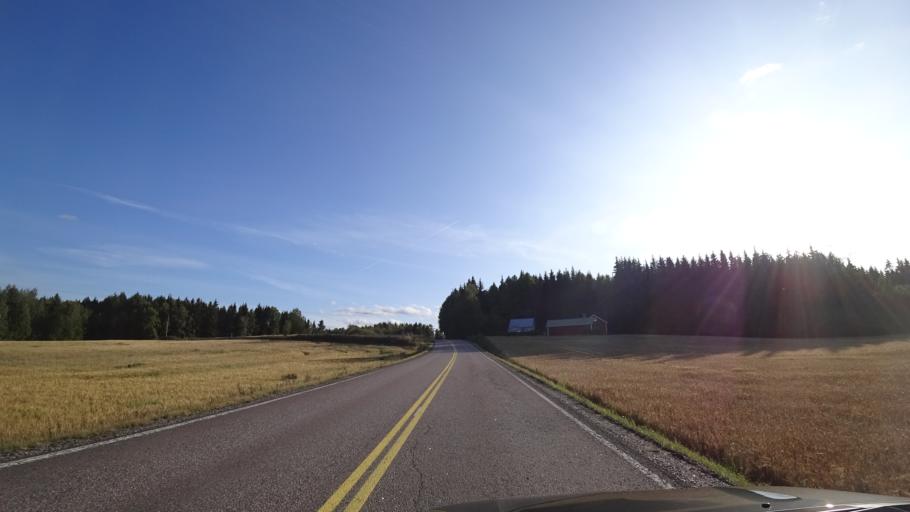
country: FI
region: Paijanne Tavastia
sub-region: Lahti
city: Asikkala
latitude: 61.1747
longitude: 25.3734
